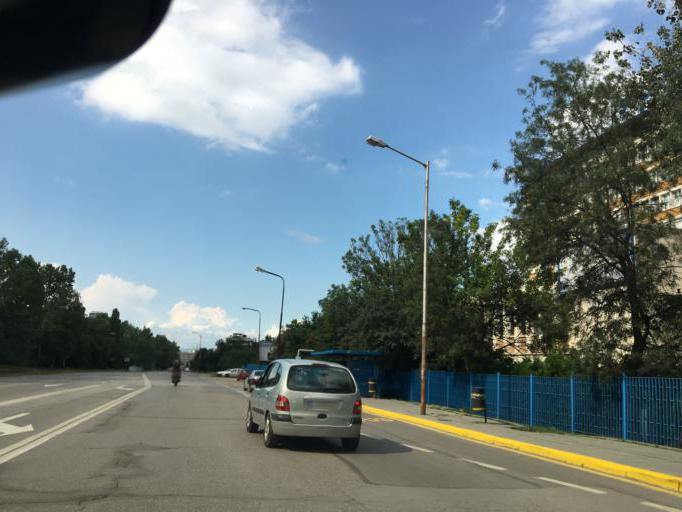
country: BG
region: Sofia-Capital
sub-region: Stolichna Obshtina
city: Sofia
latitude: 42.6574
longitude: 23.3591
